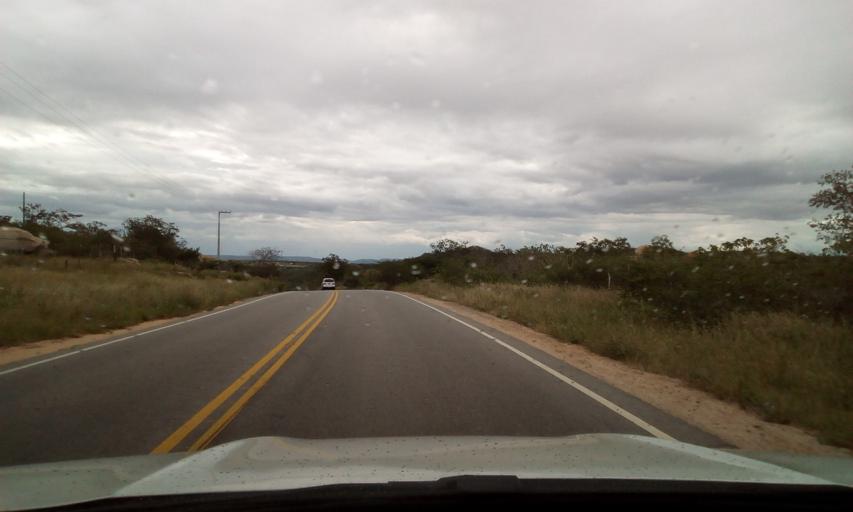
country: BR
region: Paraiba
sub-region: Picui
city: Picui
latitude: -6.5652
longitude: -36.2776
